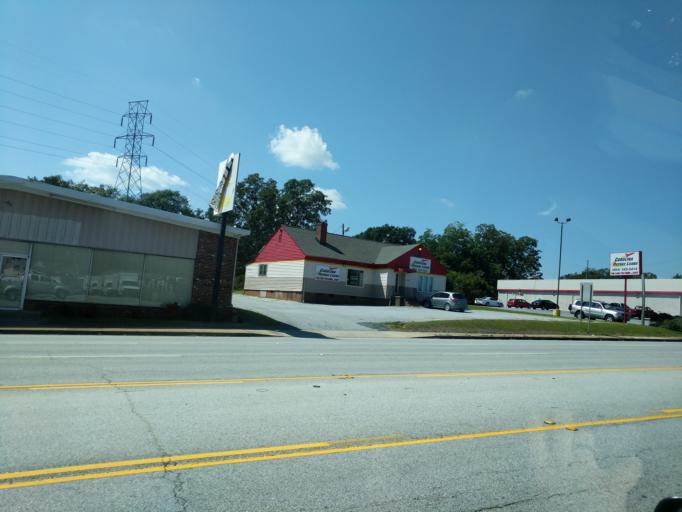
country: US
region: South Carolina
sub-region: Spartanburg County
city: Saxon
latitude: 34.9739
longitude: -81.9571
